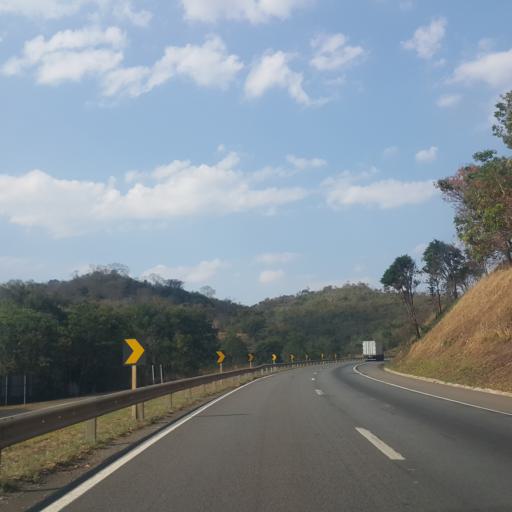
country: BR
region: Goias
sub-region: Abadiania
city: Abadiania
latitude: -16.1109
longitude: -48.5853
